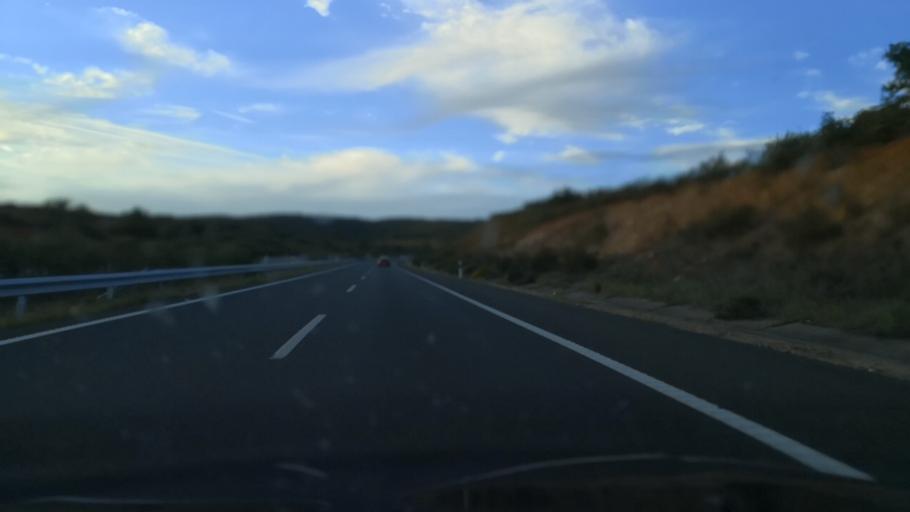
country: ES
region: Extremadura
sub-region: Provincia de Caceres
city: Alcuescar
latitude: 39.1455
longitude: -6.2745
